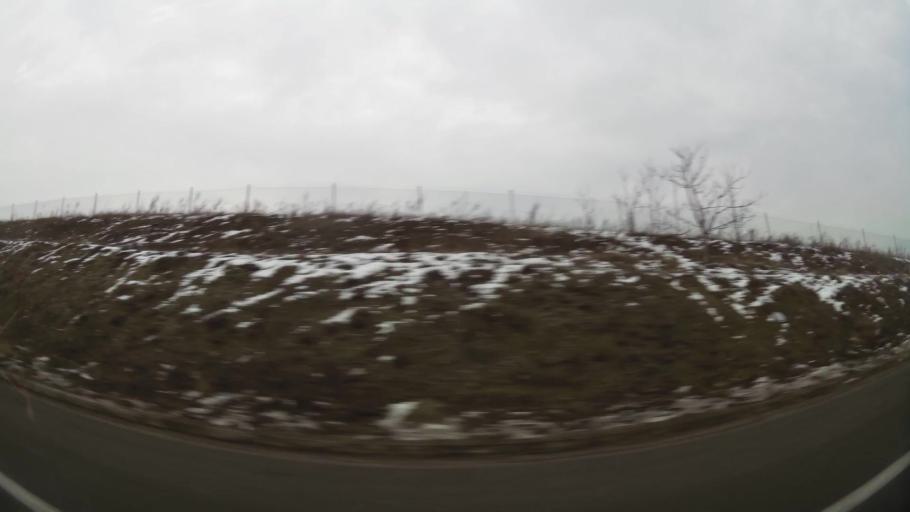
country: MK
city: Kondovo
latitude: 42.0203
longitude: 21.3312
